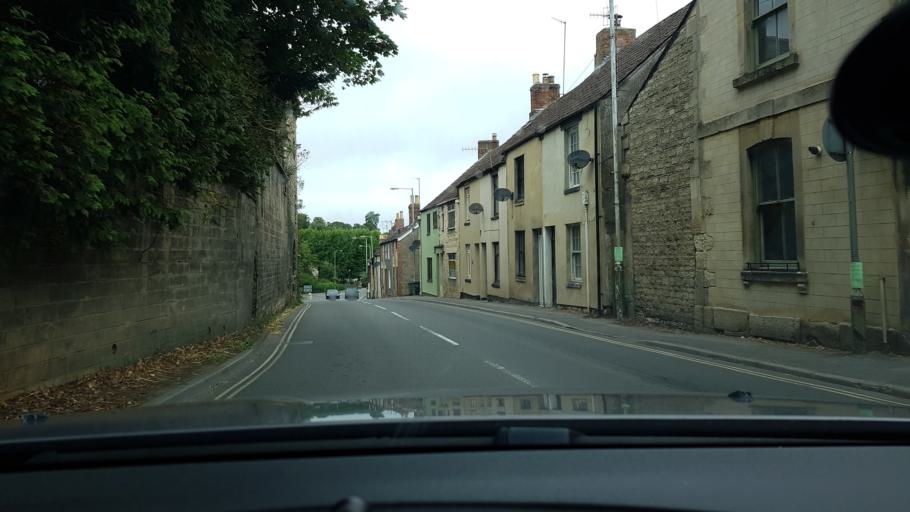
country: GB
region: England
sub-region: Wiltshire
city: Calne
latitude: 51.4354
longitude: -2.0029
